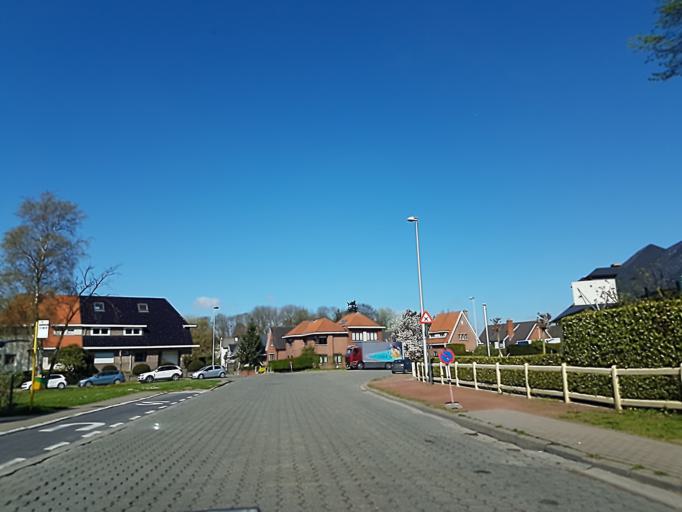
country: BE
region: Flanders
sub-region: Provincie Vlaams-Brabant
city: Dilbeek
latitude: 50.8496
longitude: 4.2663
